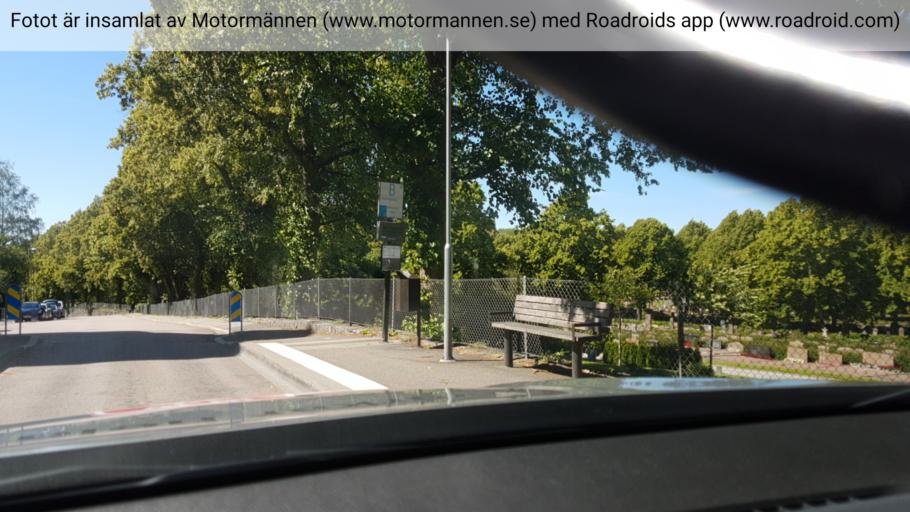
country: SE
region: Vaestra Goetaland
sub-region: Goteborg
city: Goeteborg
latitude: 57.7135
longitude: 12.0124
